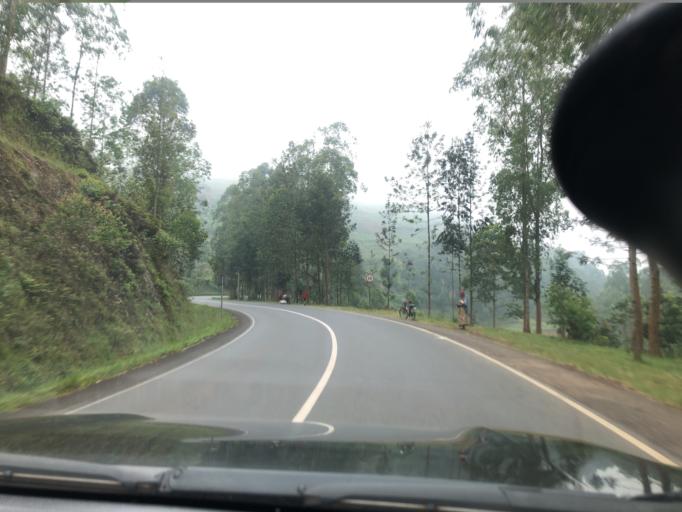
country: RW
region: Northern Province
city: Musanze
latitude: -1.5823
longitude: 29.7341
